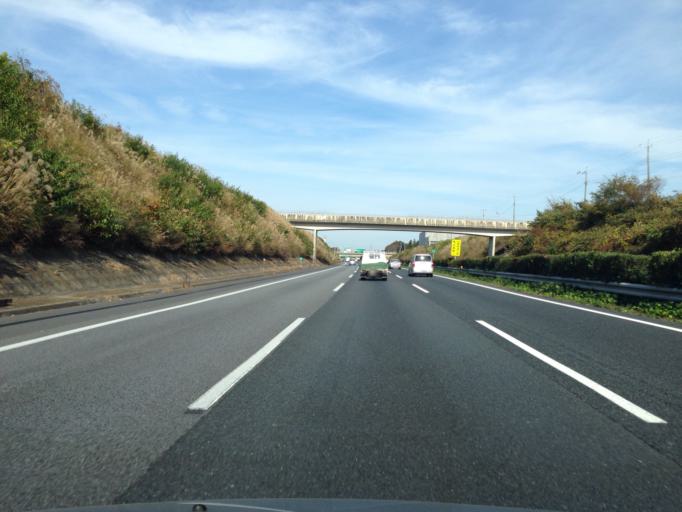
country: JP
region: Ibaraki
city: Tomobe
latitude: 36.3024
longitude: 140.3382
